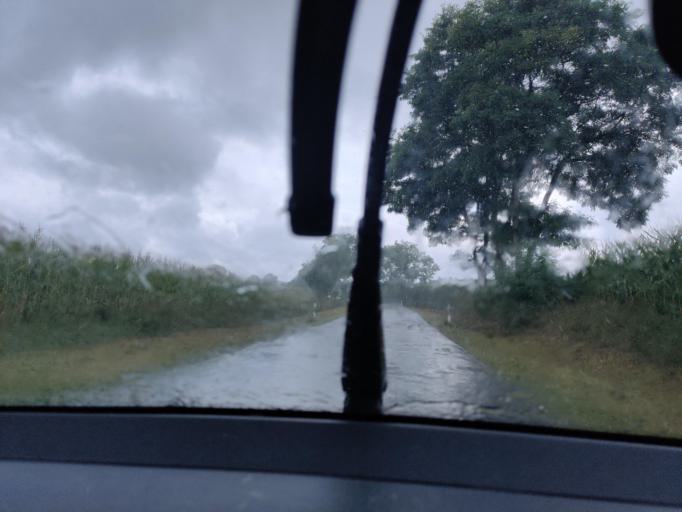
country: DE
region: Mecklenburg-Vorpommern
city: Wesenberg
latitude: 53.2735
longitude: 12.9943
